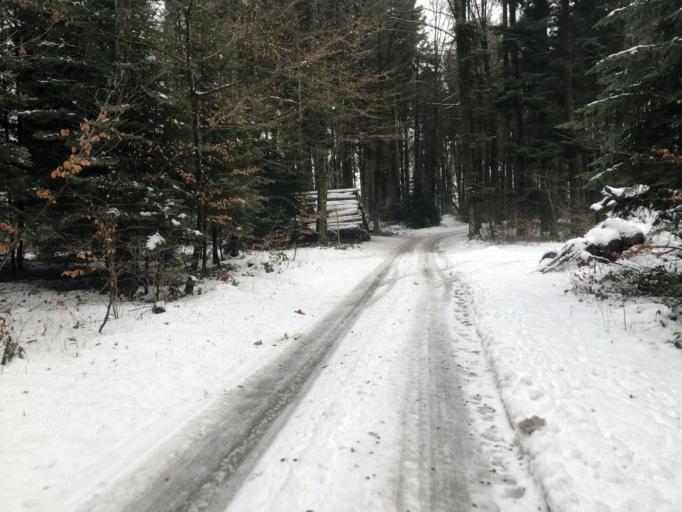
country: CH
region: Bern
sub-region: Oberaargau
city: Herzogenbuchsee
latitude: 47.1943
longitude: 7.7406
